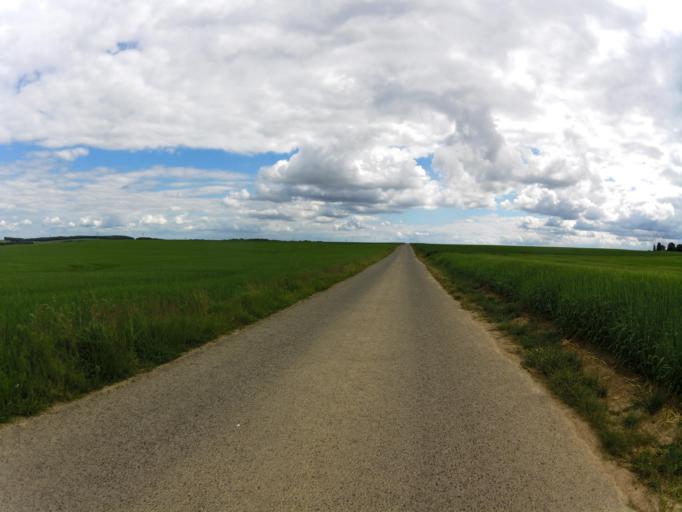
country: DE
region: Bavaria
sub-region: Regierungsbezirk Unterfranken
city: Gaukonigshofen
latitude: 49.6529
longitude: 10.0043
